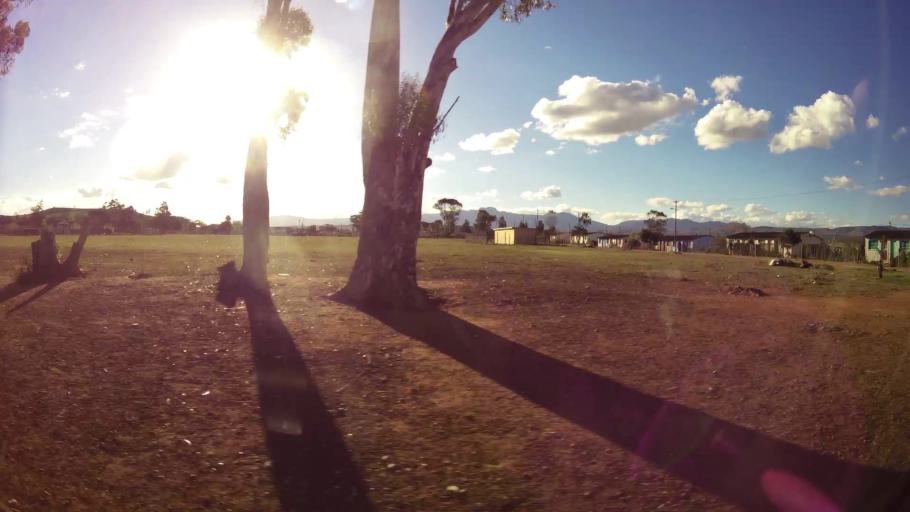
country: ZA
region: Western Cape
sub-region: Eden District Municipality
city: Riversdale
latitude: -34.1036
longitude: 20.9651
